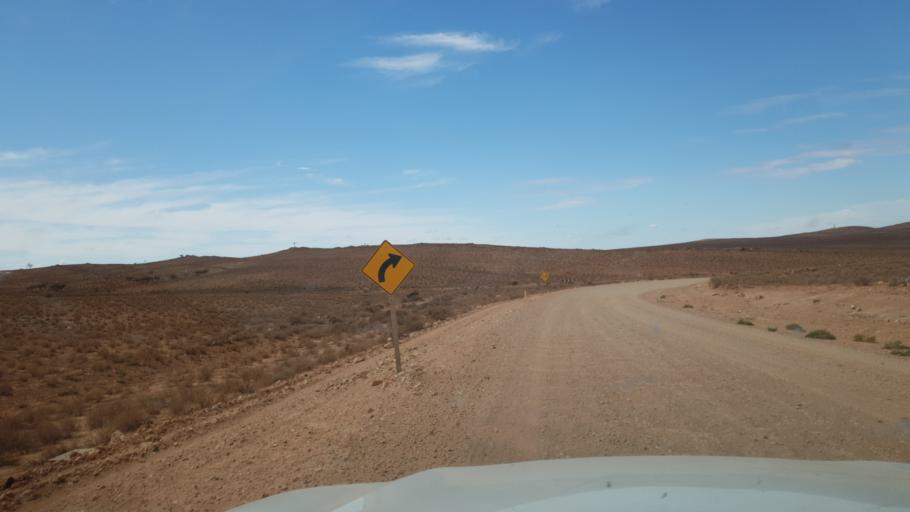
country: AU
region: South Australia
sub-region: Peterborough
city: Peterborough
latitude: -32.2649
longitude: 139.4217
